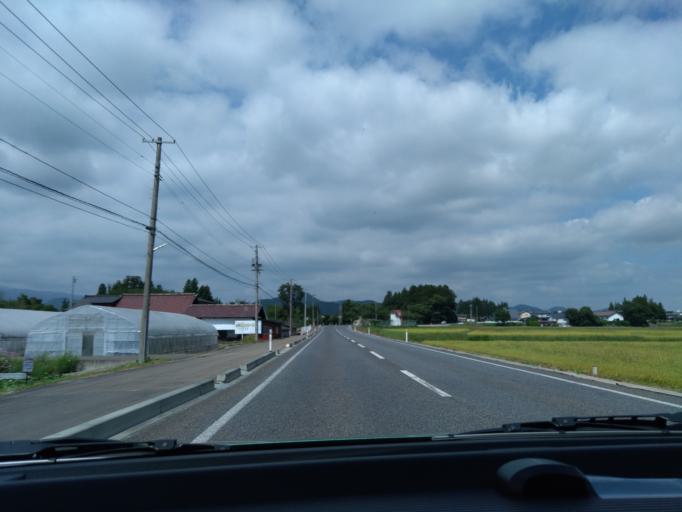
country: JP
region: Iwate
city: Hanamaki
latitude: 39.3827
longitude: 141.0558
